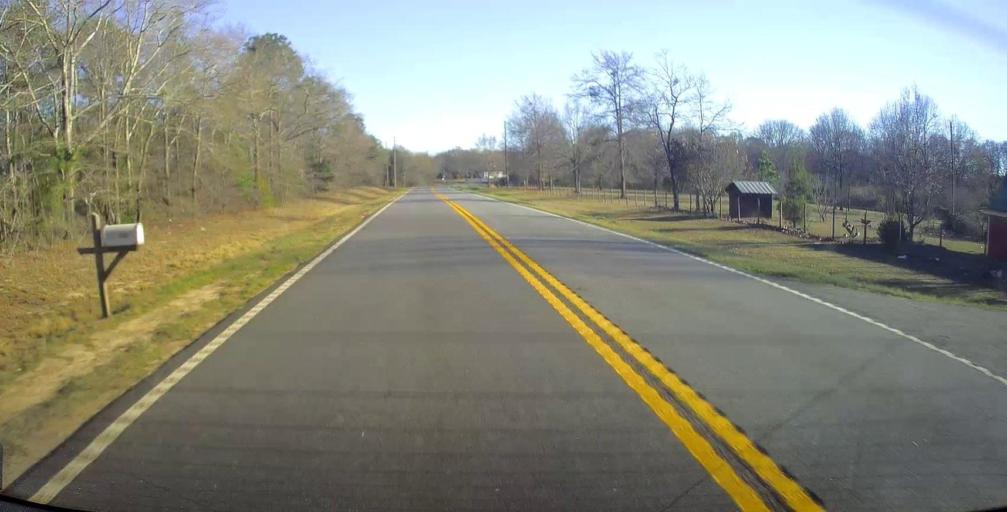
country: US
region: Georgia
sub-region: Taylor County
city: Butler
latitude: 32.5059
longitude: -84.4220
